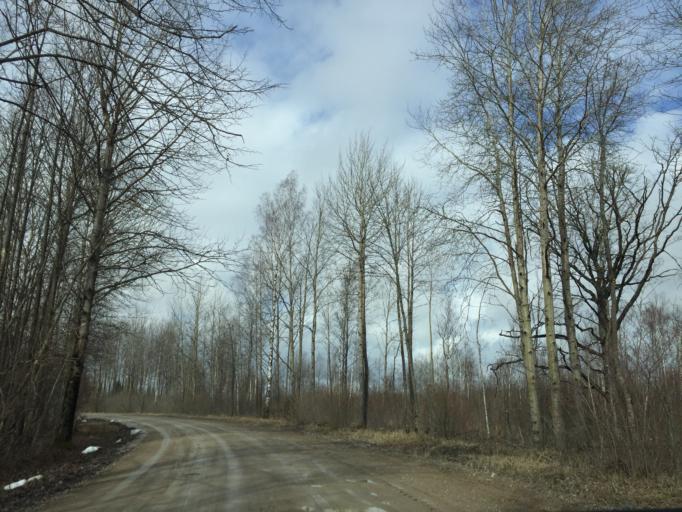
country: EE
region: Laeaene
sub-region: Lihula vald
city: Lihula
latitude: 58.7326
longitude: 23.8303
